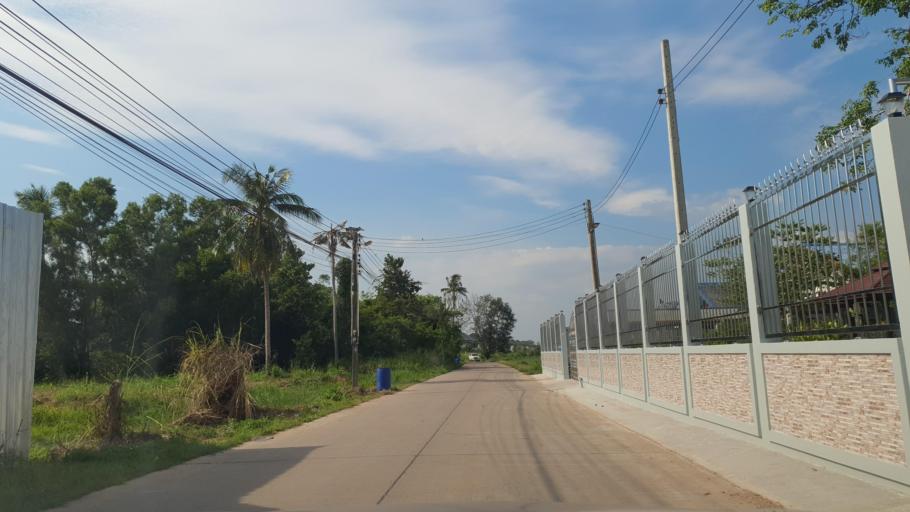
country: TH
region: Chon Buri
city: Sattahip
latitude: 12.7983
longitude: 100.9352
